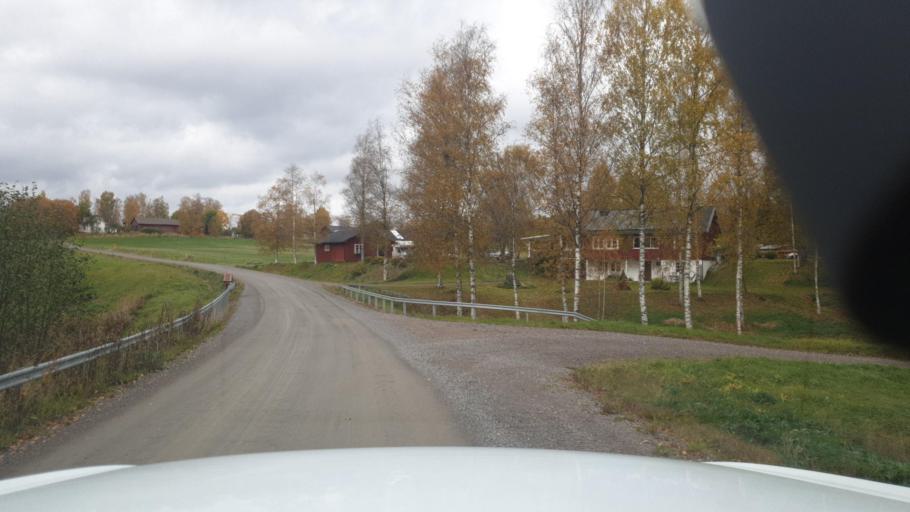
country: SE
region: Vaermland
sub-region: Sunne Kommun
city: Sunne
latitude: 59.8112
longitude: 13.0633
